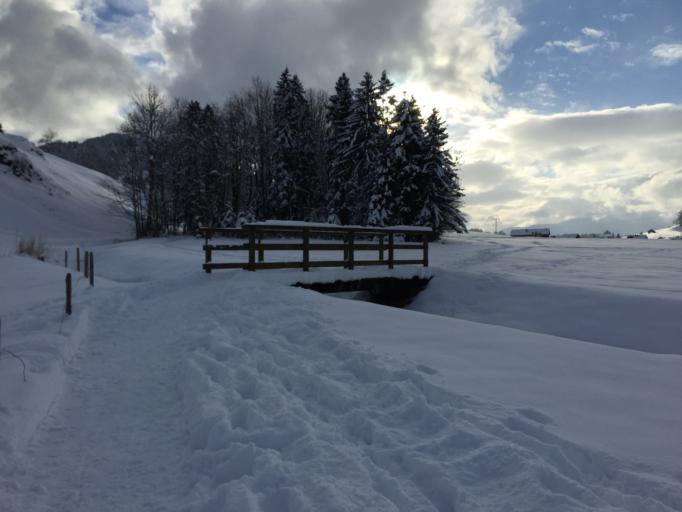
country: CH
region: Schwyz
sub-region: Bezirk Schwyz
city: Rothenthurm
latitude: 47.0971
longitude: 8.6772
